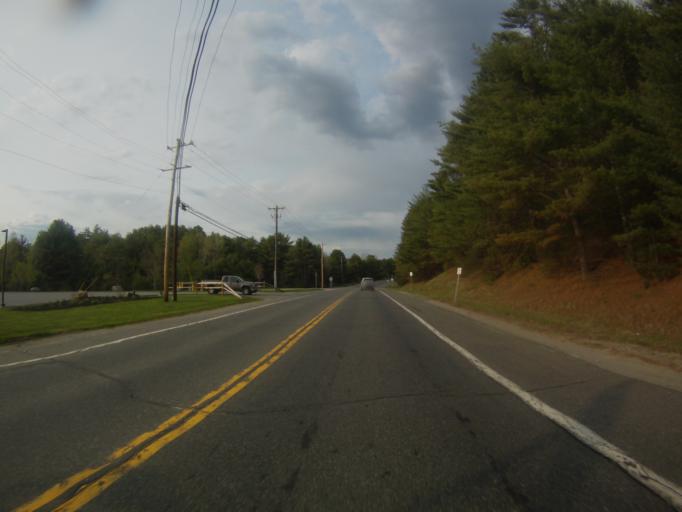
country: US
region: New York
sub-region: Warren County
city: Warrensburg
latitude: 43.6651
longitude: -73.7843
